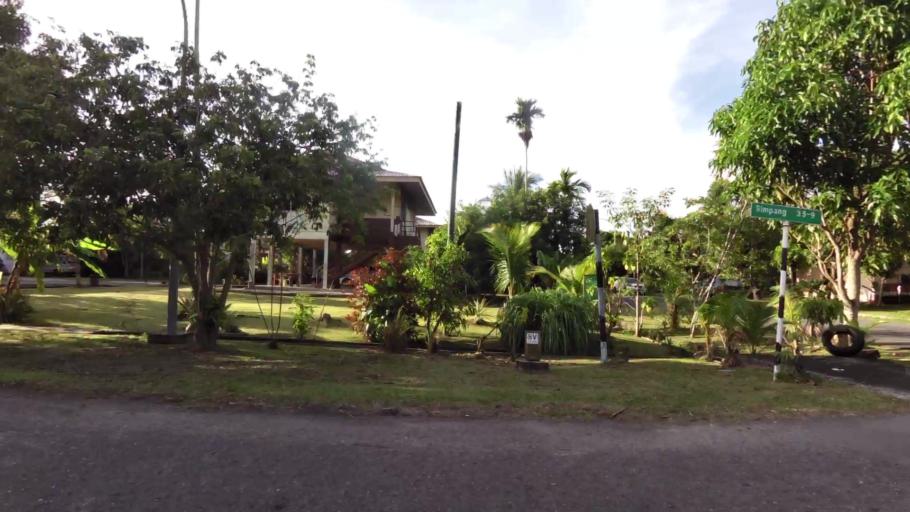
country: BN
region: Belait
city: Kuala Belait
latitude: 4.5767
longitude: 114.2236
